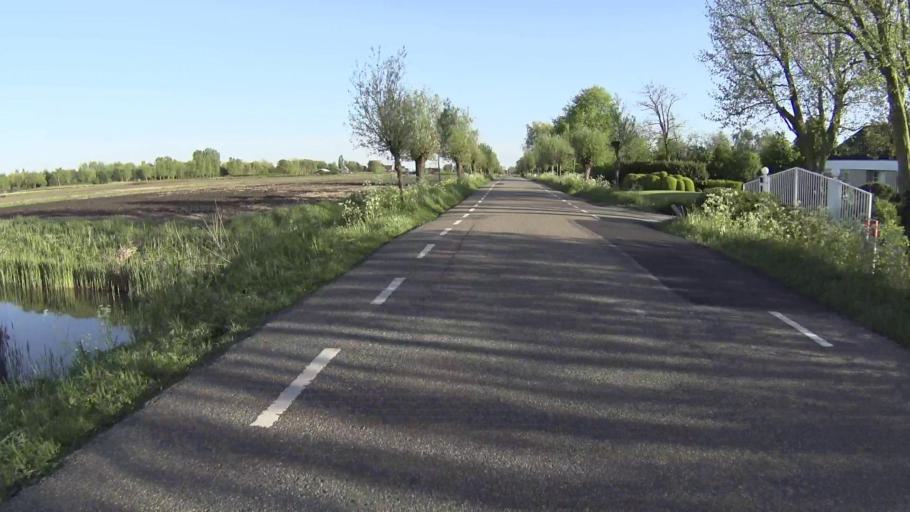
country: NL
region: South Holland
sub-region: Gemeente Rijnwoude
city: Benthuizen
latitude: 52.1010
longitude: 4.5558
